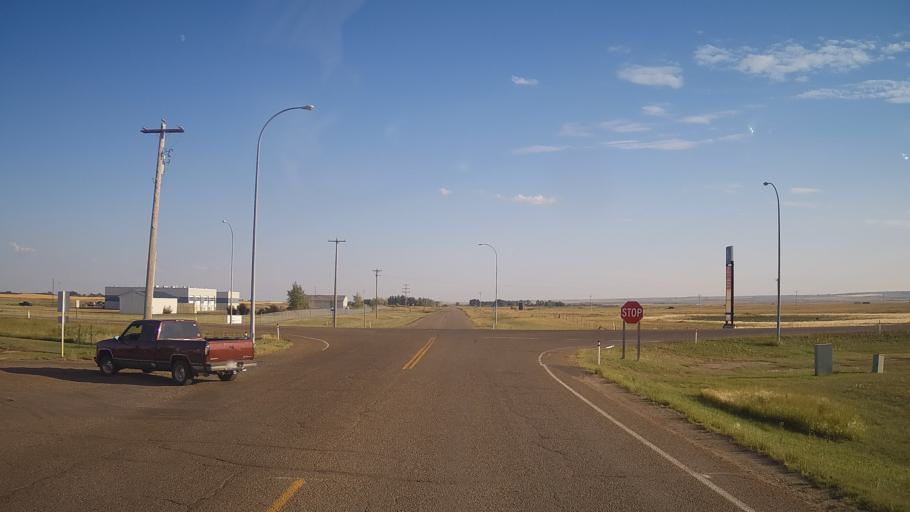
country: CA
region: Alberta
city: Hanna
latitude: 51.6348
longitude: -111.9422
